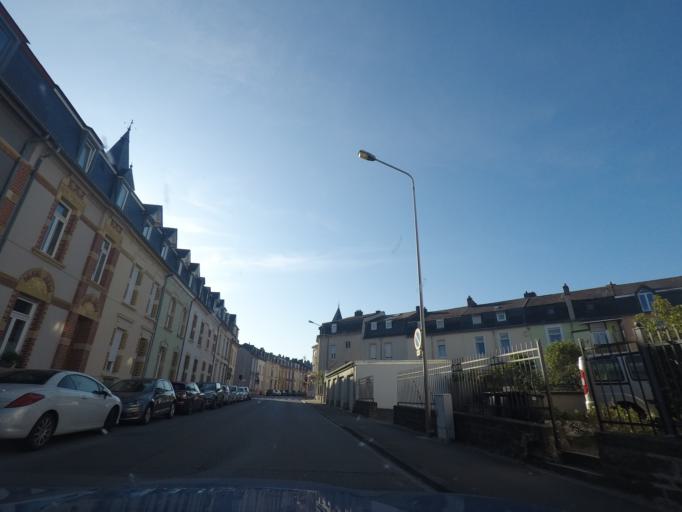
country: LU
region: Luxembourg
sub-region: Canton de Luxembourg
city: Luxembourg
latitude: 49.5959
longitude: 6.1394
